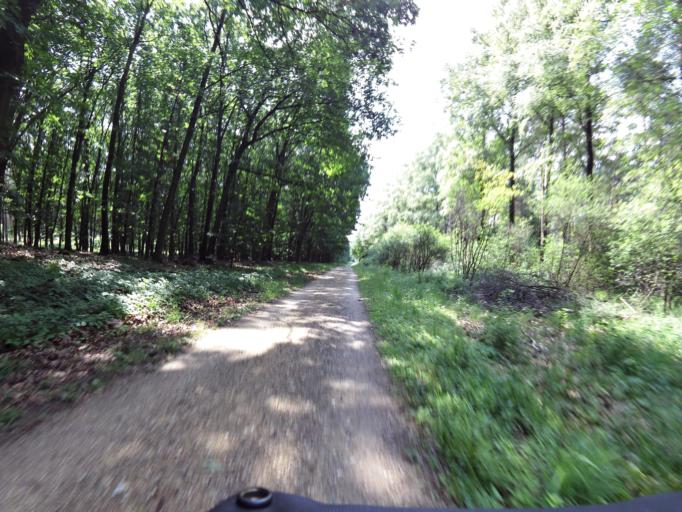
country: DE
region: North Rhine-Westphalia
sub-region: Regierungsbezirk Dusseldorf
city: Niederkruchten
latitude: 51.1653
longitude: 6.1829
